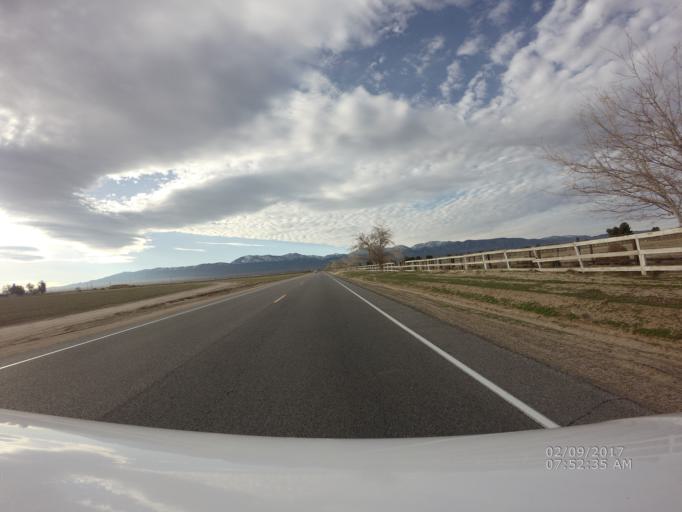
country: US
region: California
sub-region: Los Angeles County
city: Lake Los Angeles
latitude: 34.5612
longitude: -117.8265
